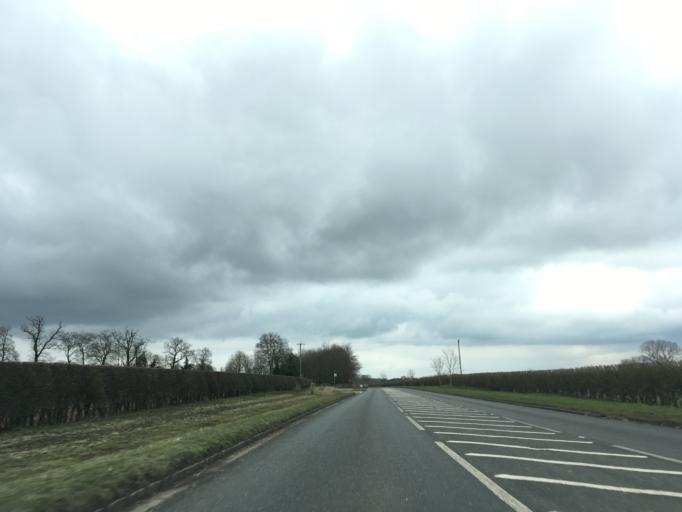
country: GB
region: England
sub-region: West Berkshire
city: Kintbury
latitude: 51.4143
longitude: -1.4367
